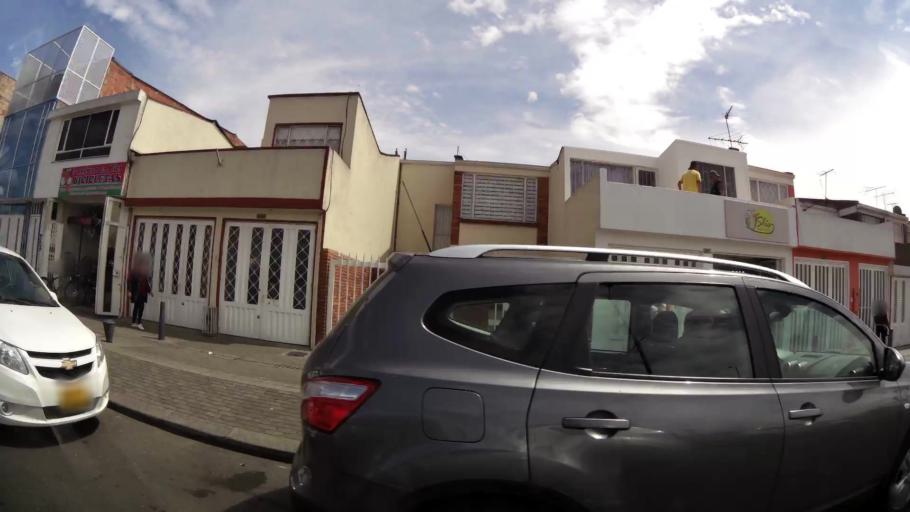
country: CO
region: Bogota D.C.
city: Bogota
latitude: 4.6295
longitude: -74.1344
